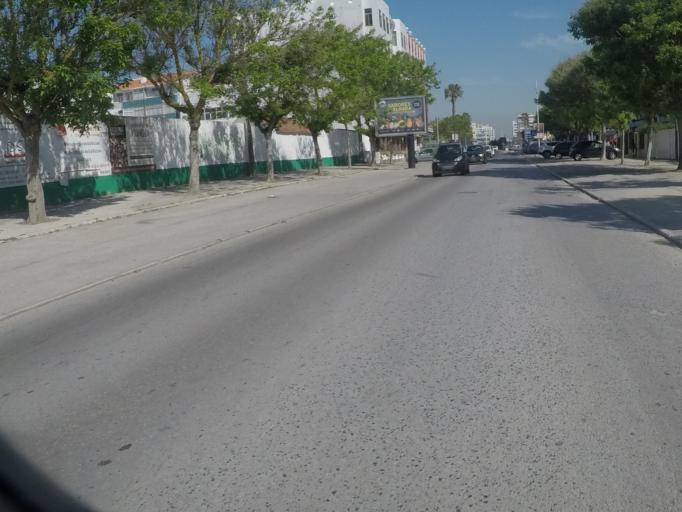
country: PT
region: Setubal
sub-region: Almada
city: Costa de Caparica
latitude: 38.6377
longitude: -9.2297
